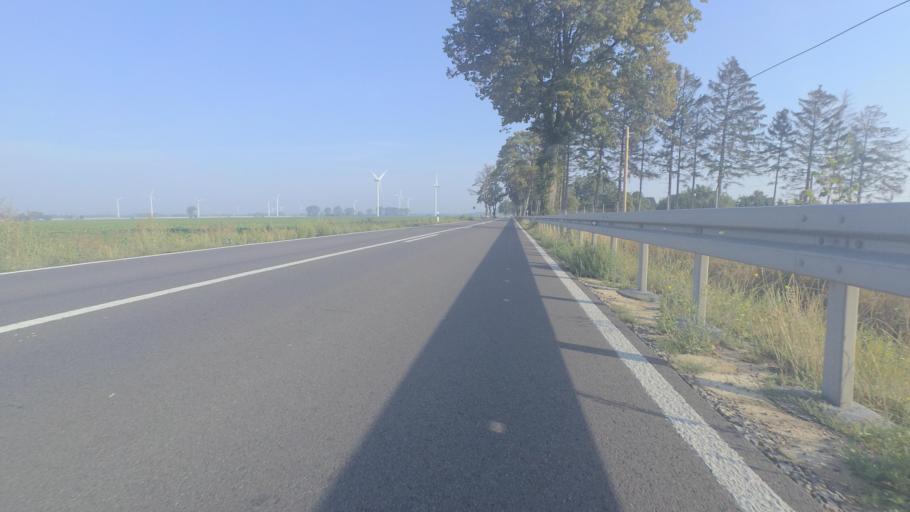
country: DE
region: Mecklenburg-Vorpommern
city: Gormin
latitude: 53.9982
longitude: 13.1465
